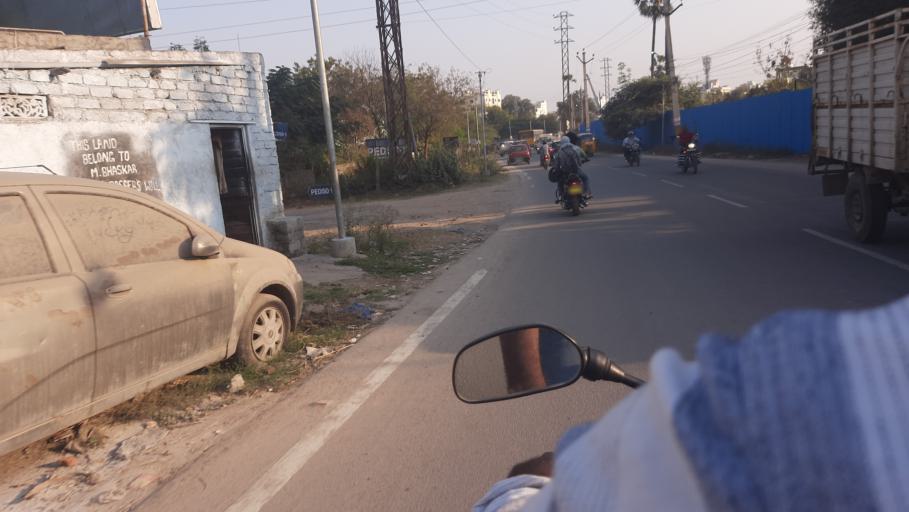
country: IN
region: Telangana
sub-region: Rangareddi
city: Secunderabad
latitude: 17.5114
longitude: 78.5403
